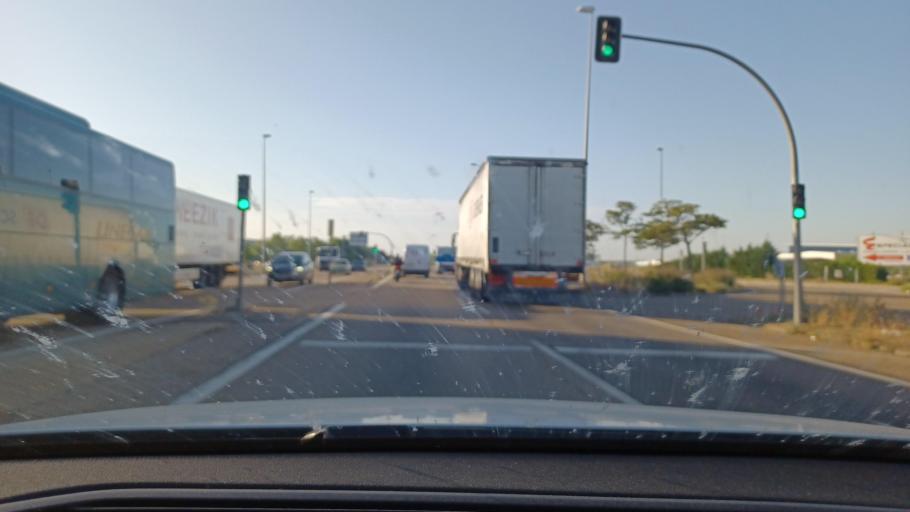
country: ES
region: Castille and Leon
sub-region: Provincia de Valladolid
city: Cisterniga
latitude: 41.6075
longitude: -4.7076
